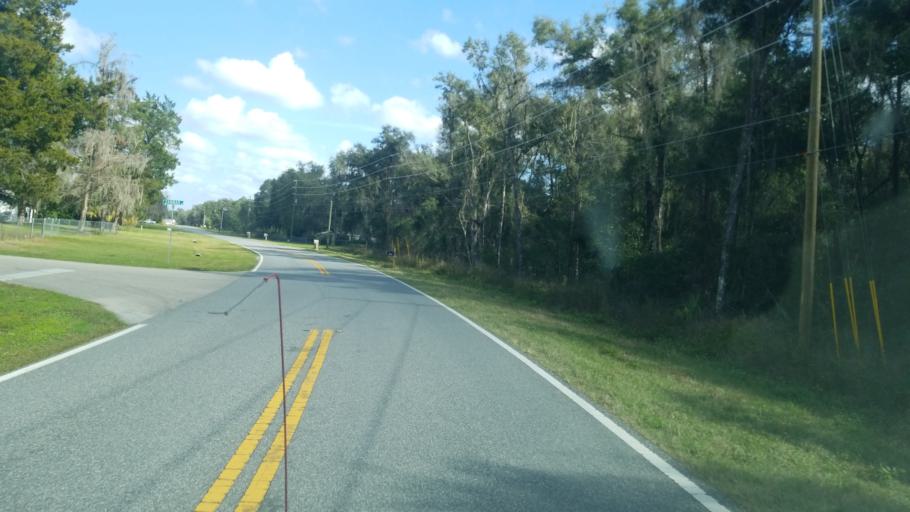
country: US
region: Florida
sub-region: Citrus County
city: Floral City
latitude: 28.7281
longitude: -82.3087
